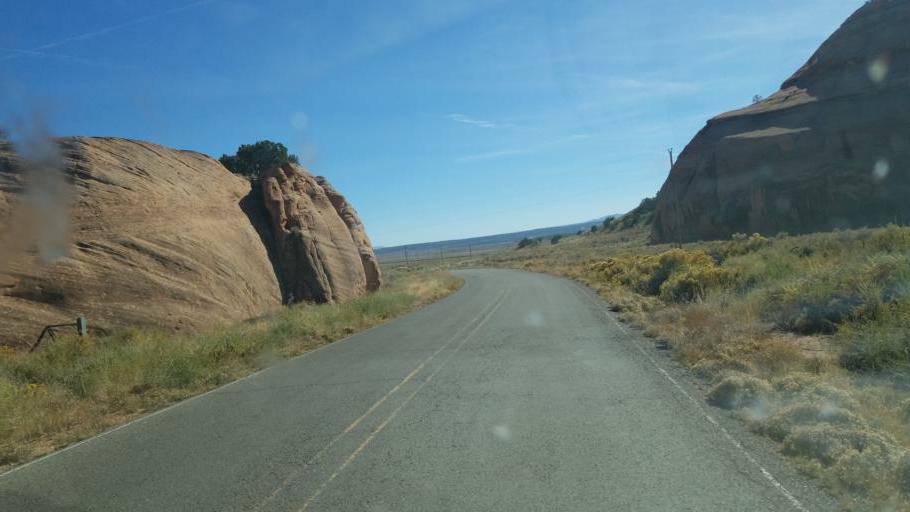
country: US
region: New Mexico
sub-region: McKinley County
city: Thoreau
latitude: 35.4341
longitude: -108.0512
